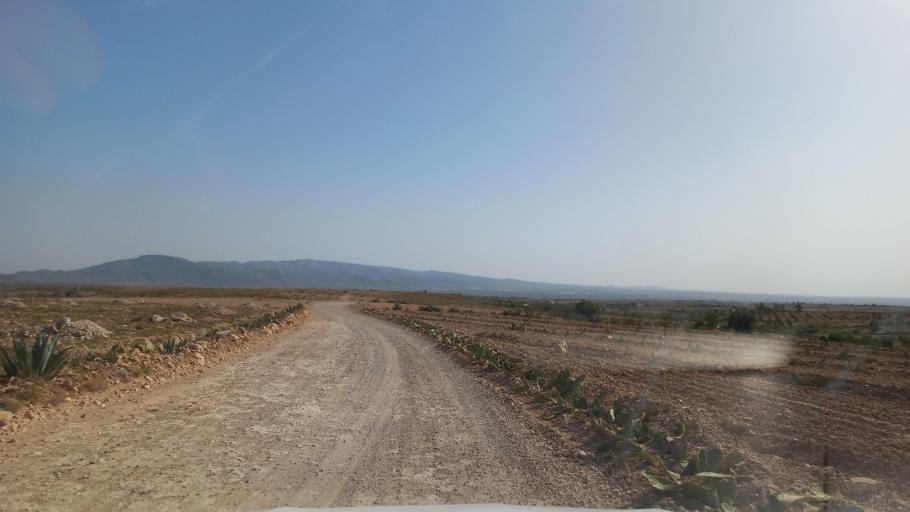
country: TN
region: Al Qasrayn
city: Kasserine
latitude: 35.2597
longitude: 8.9247
